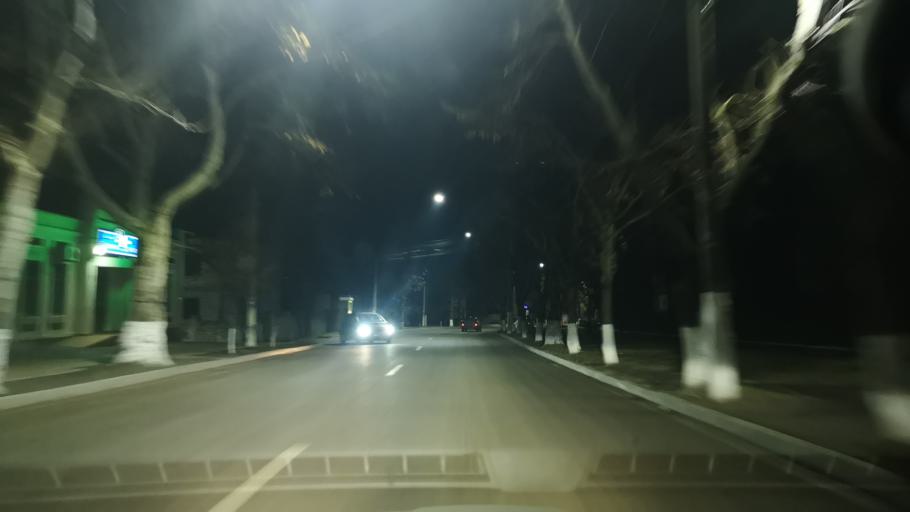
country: MD
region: Orhei
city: Orhei
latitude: 47.3858
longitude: 28.8251
